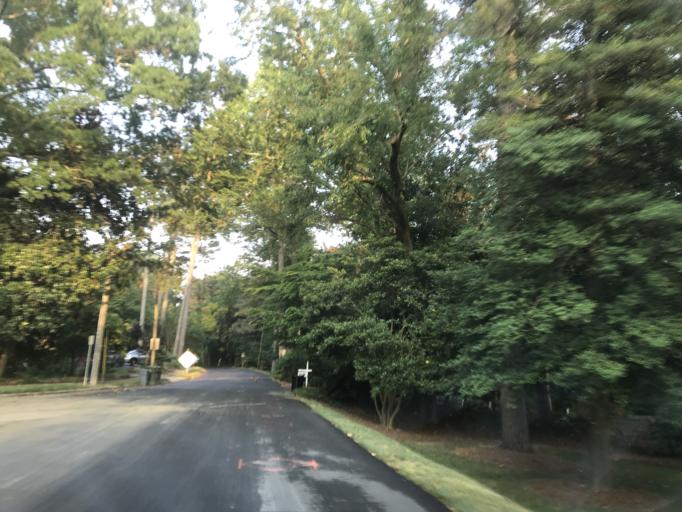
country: US
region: North Carolina
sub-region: Wake County
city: West Raleigh
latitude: 35.7986
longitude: -78.6497
